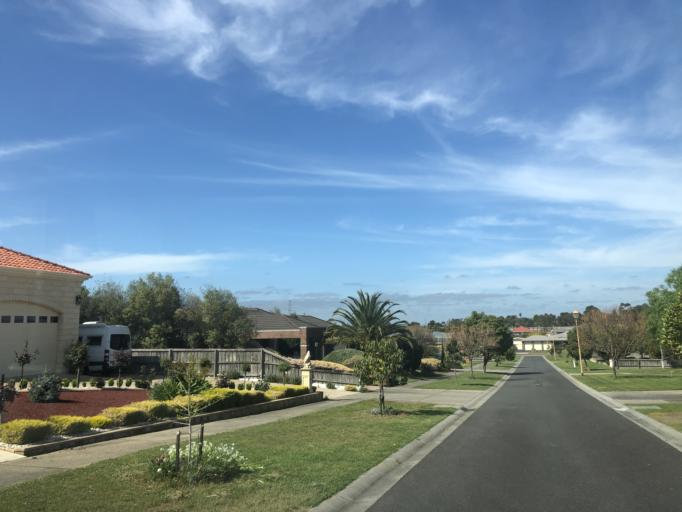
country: AU
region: Victoria
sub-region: Casey
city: Hallam
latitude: -37.9952
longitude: 145.2838
